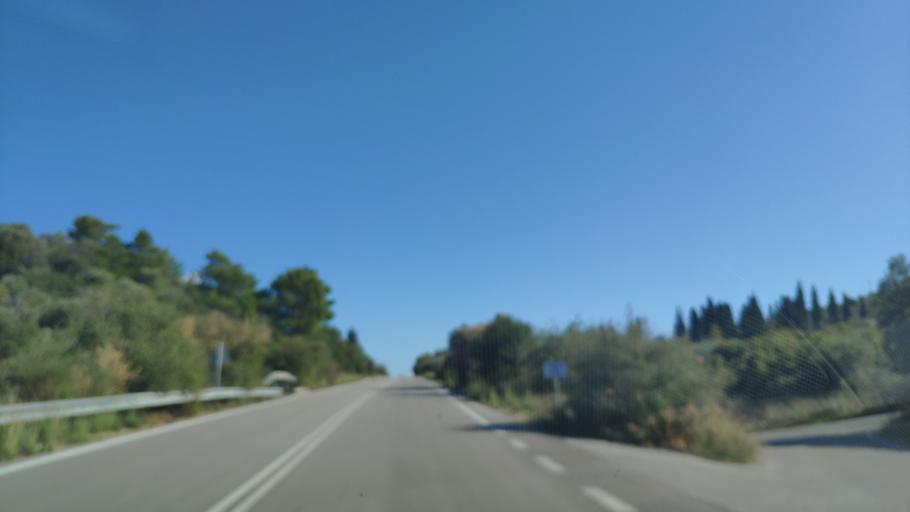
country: GR
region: Peloponnese
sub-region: Nomos Argolidos
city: Palaia Epidavros
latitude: 37.5769
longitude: 23.2431
